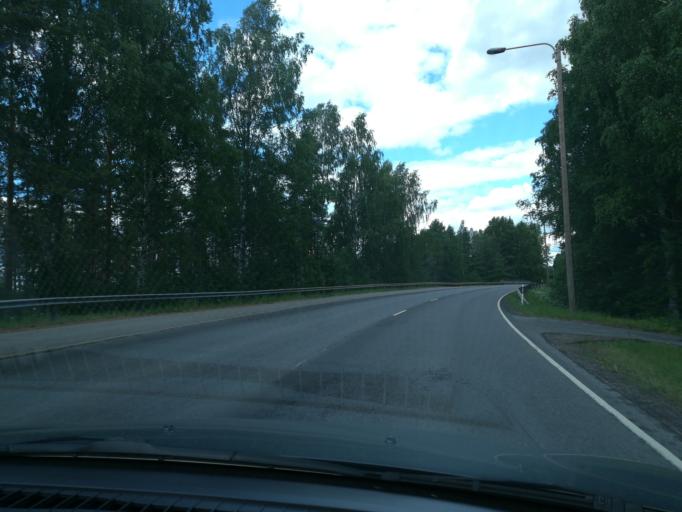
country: FI
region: Southern Savonia
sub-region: Mikkeli
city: Maentyharju
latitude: 61.4265
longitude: 26.8917
